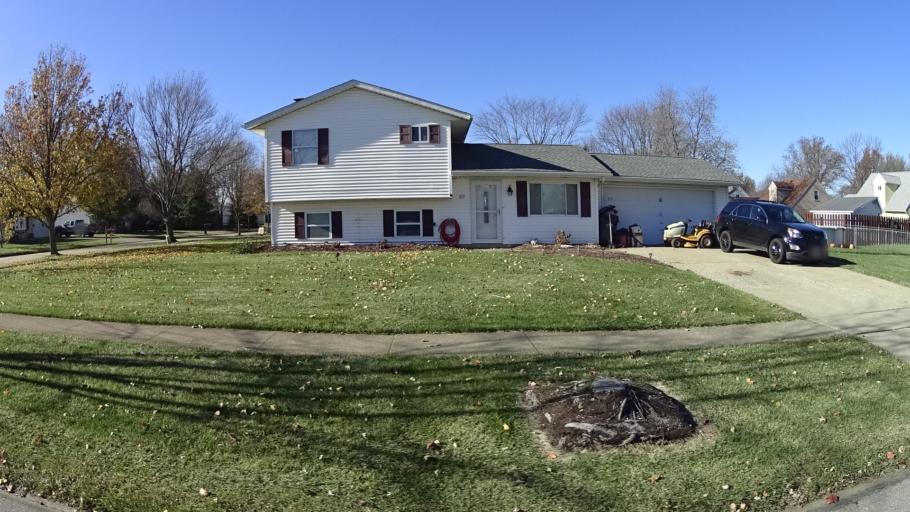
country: US
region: Ohio
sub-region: Lorain County
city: Elyria
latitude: 41.3467
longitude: -82.0711
